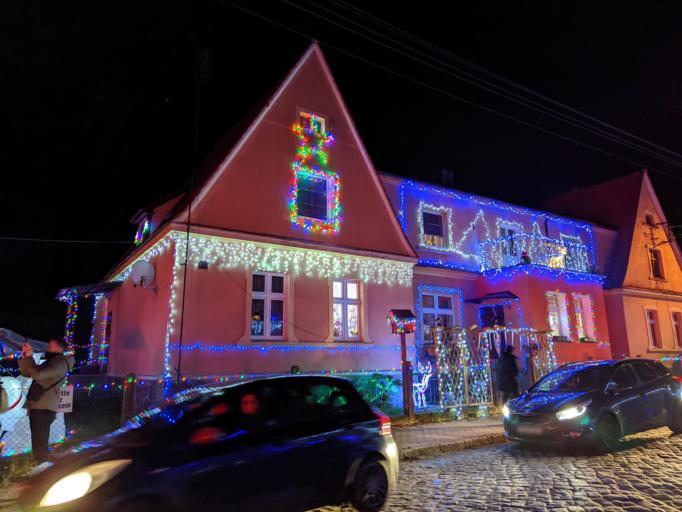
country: PL
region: Lubusz
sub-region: Powiat miedzyrzecki
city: Skwierzyna
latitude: 52.5326
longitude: 15.5131
